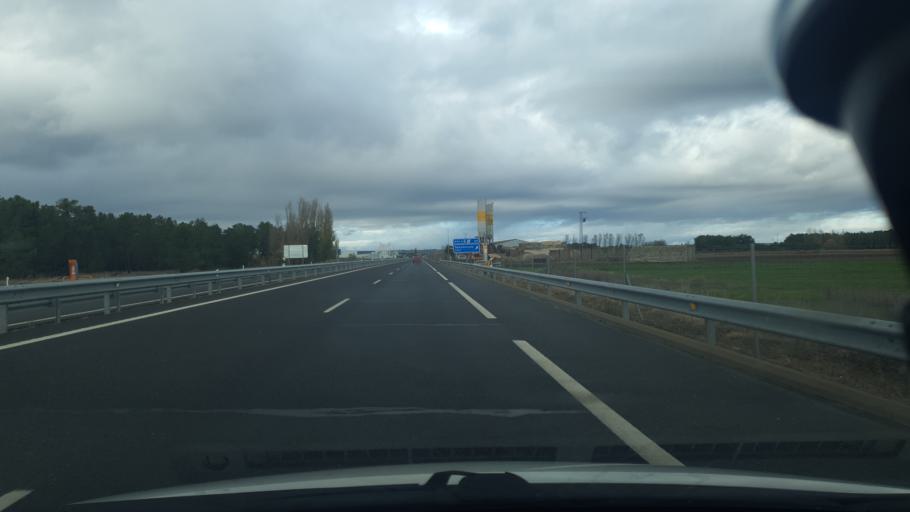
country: ES
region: Castille and Leon
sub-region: Provincia de Segovia
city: Sanchonuno
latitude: 41.3050
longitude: -4.3025
